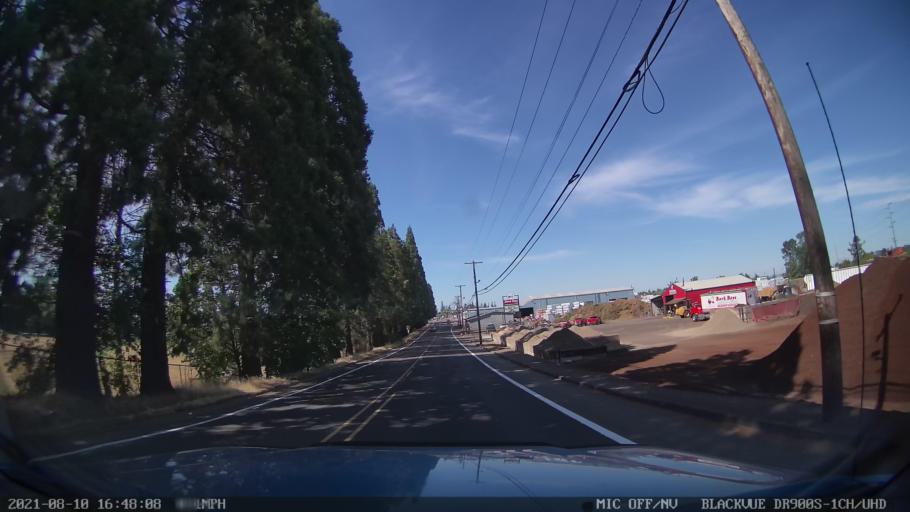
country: US
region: Oregon
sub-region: Marion County
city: Keizer
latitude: 44.9667
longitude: -123.0194
